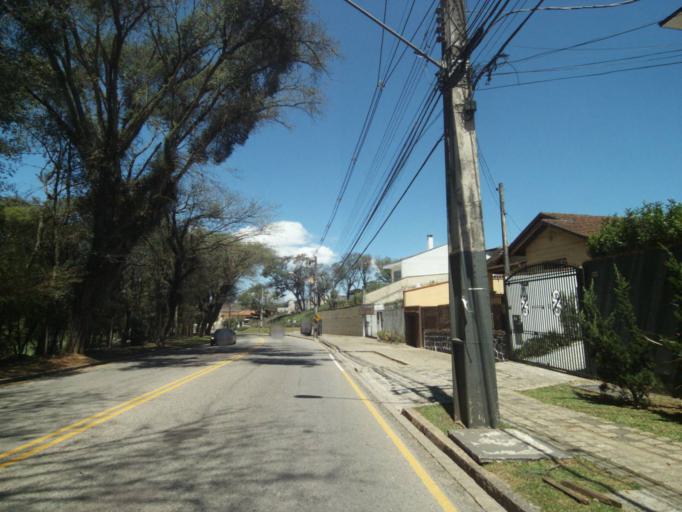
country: BR
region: Parana
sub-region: Curitiba
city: Curitiba
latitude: -25.3849
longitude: -49.2679
